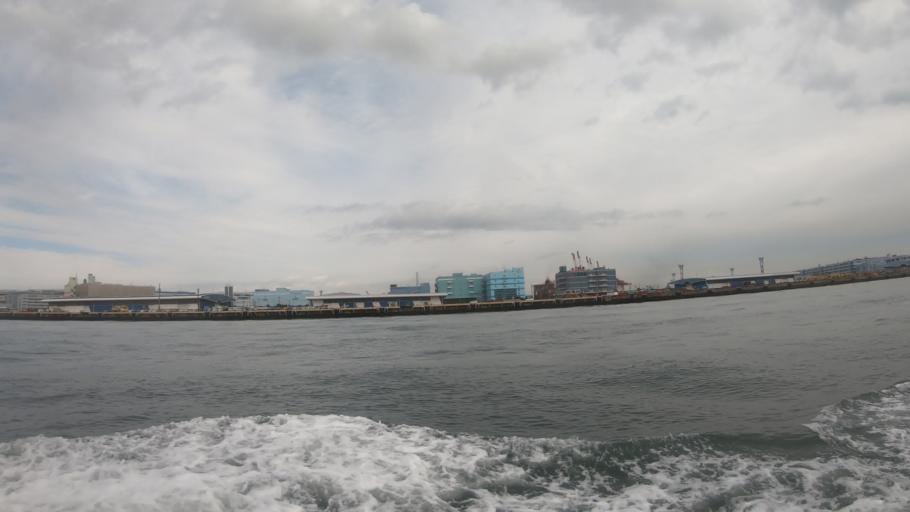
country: JP
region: Kanagawa
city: Yokohama
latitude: 35.4534
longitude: 139.6842
